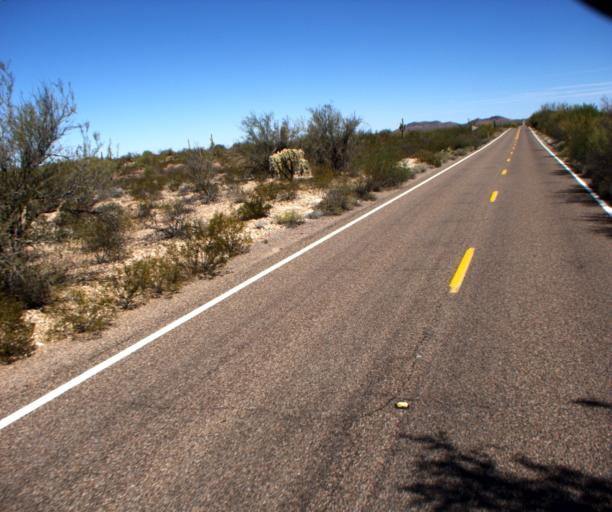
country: MX
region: Sonora
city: Sonoyta
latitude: 32.0288
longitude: -112.8000
